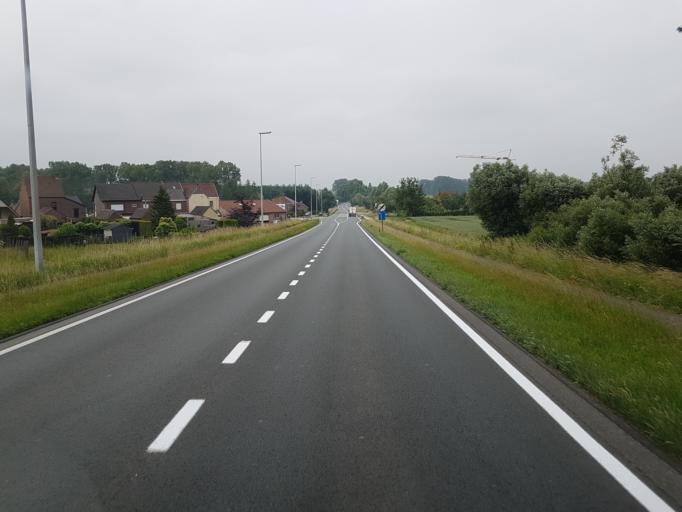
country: BE
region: Flanders
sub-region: Provincie Oost-Vlaanderen
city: Sint-Maria-Lierde
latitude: 50.8076
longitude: 3.8716
